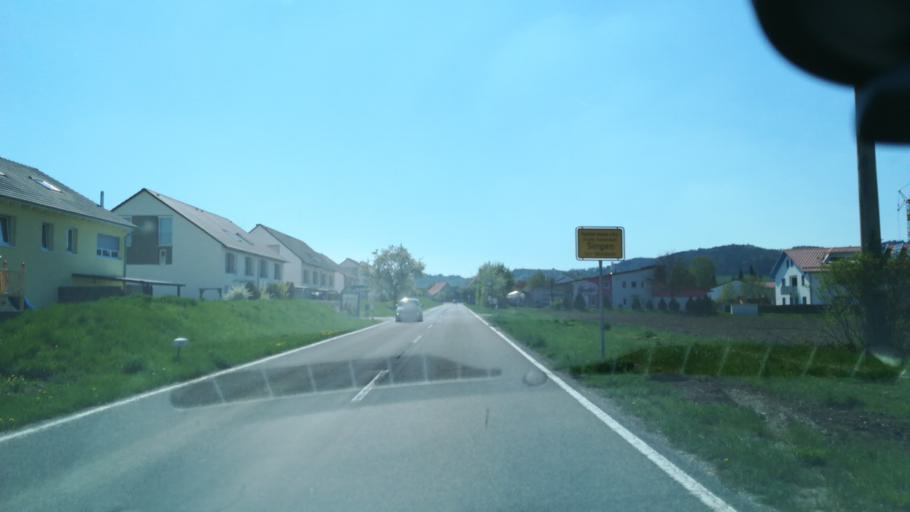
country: DE
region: Baden-Wuerttemberg
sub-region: Freiburg Region
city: Volkertshausen
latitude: 47.7955
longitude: 8.8442
